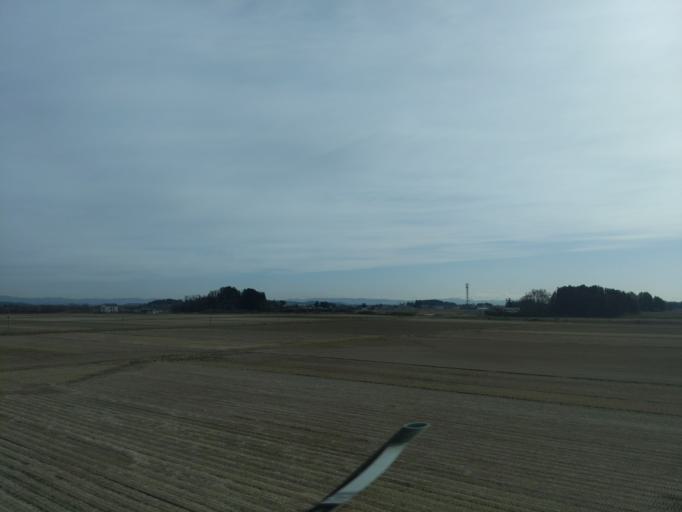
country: JP
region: Iwate
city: Ichinoseki
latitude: 38.7791
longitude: 141.0889
